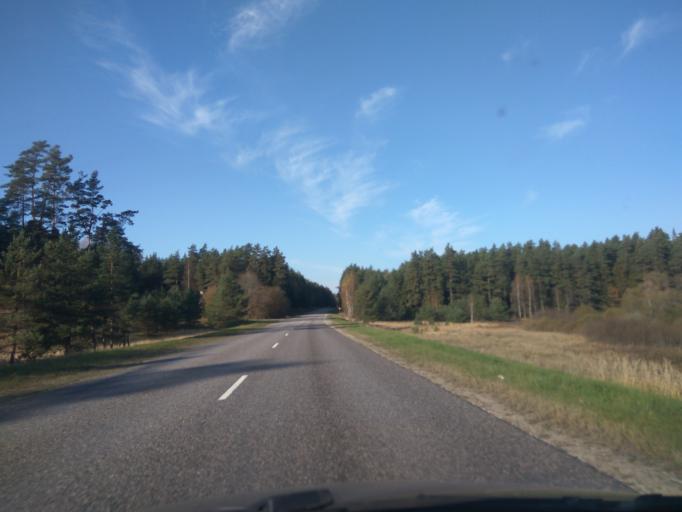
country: LV
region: Ventspils Rajons
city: Piltene
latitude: 57.0762
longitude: 21.7904
